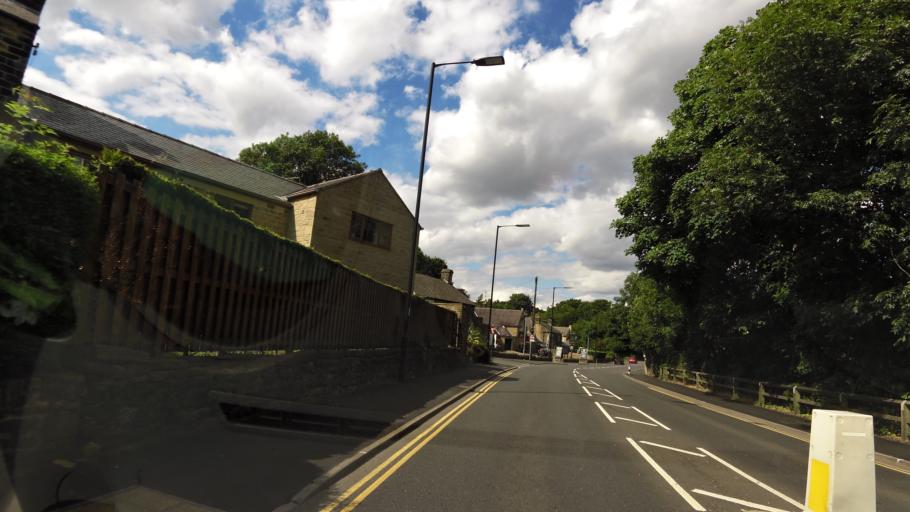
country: GB
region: England
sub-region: Sheffield
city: Chapletown
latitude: 53.4404
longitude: -1.4963
